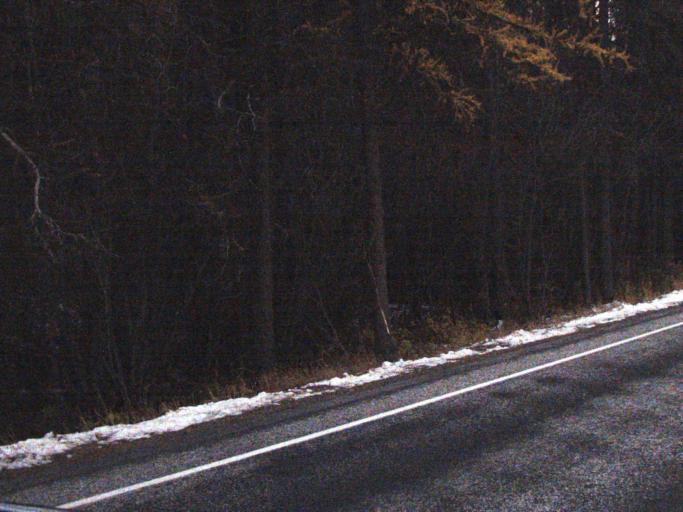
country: US
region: Washington
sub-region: Ferry County
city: Republic
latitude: 48.6226
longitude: -118.4263
